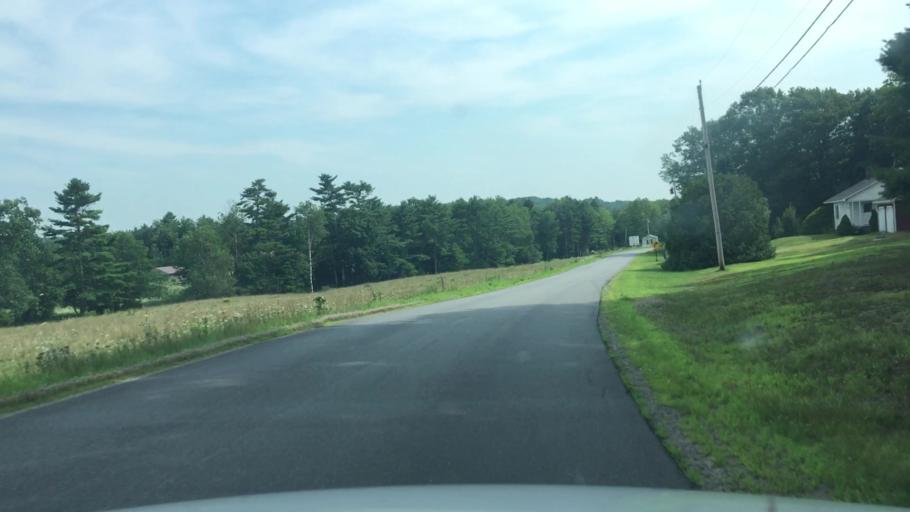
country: US
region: Maine
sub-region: Lincoln County
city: Jefferson
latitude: 44.2155
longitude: -69.4476
